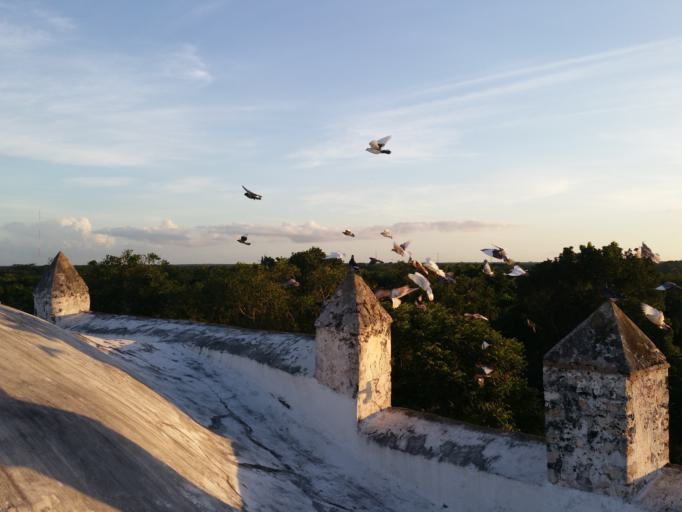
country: MX
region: Yucatan
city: Valladolid
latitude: 20.6858
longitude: -88.2099
